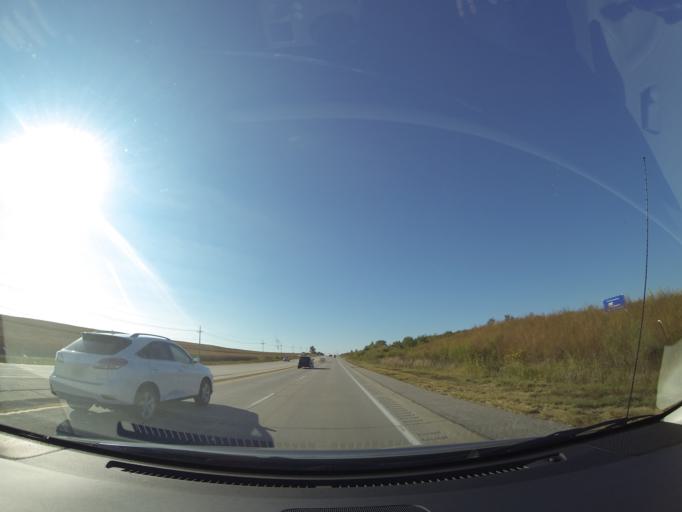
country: US
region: Nebraska
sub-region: Sarpy County
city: Gretna
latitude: 41.1975
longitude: -96.2344
